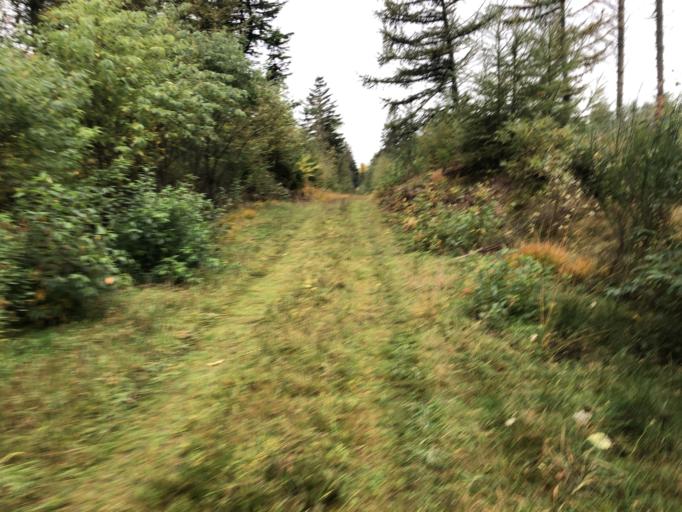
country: DK
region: Central Jutland
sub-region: Holstebro Kommune
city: Ulfborg
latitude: 56.2711
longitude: 8.4383
